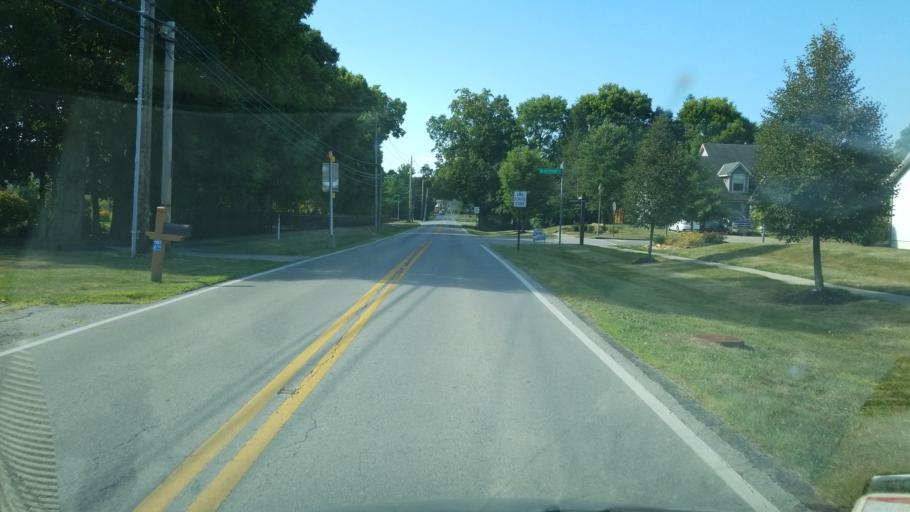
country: US
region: Ohio
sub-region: Franklin County
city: Worthington
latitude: 40.1102
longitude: -83.0426
